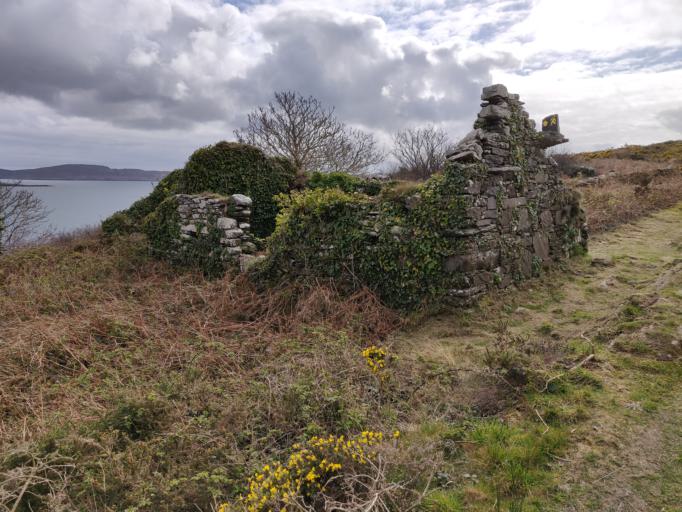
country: IE
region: Munster
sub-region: County Cork
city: Bantry
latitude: 51.5823
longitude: -9.6788
